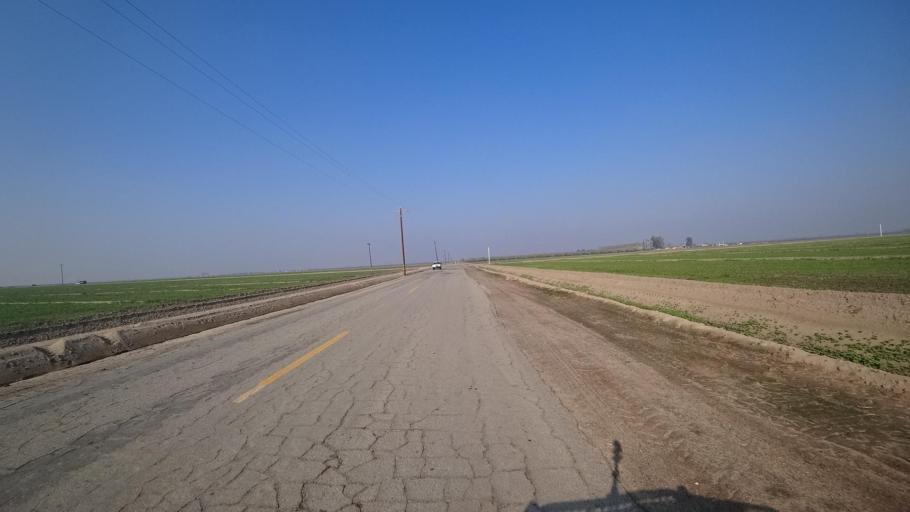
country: US
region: California
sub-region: Kern County
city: Greenfield
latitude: 35.1856
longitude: -119.0436
